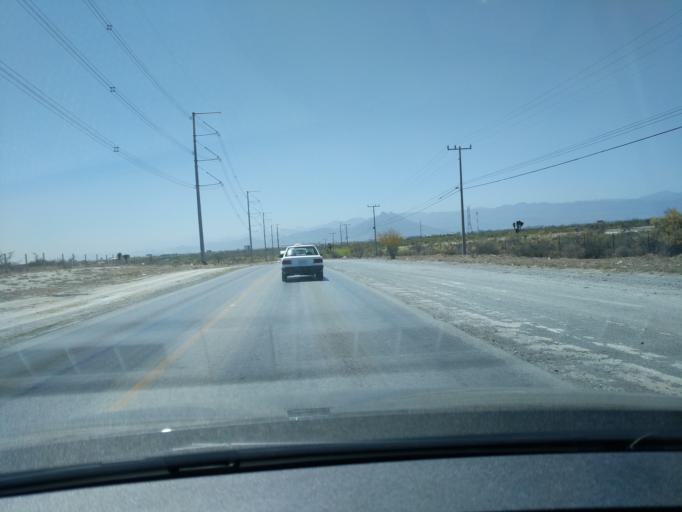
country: MX
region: Nuevo Leon
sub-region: Apodaca
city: Artemio Trevino
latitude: 25.8252
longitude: -100.1439
